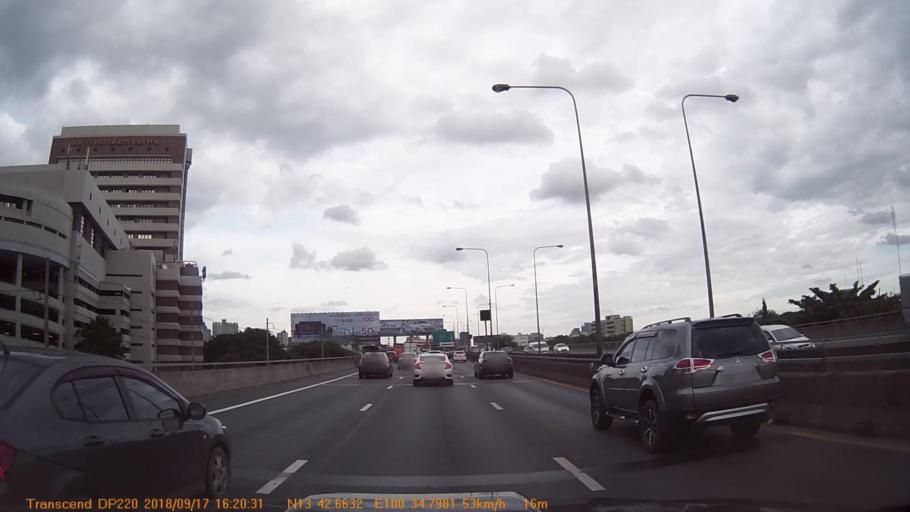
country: TH
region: Bangkok
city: Khlong Toei
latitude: 13.7080
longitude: 100.5807
